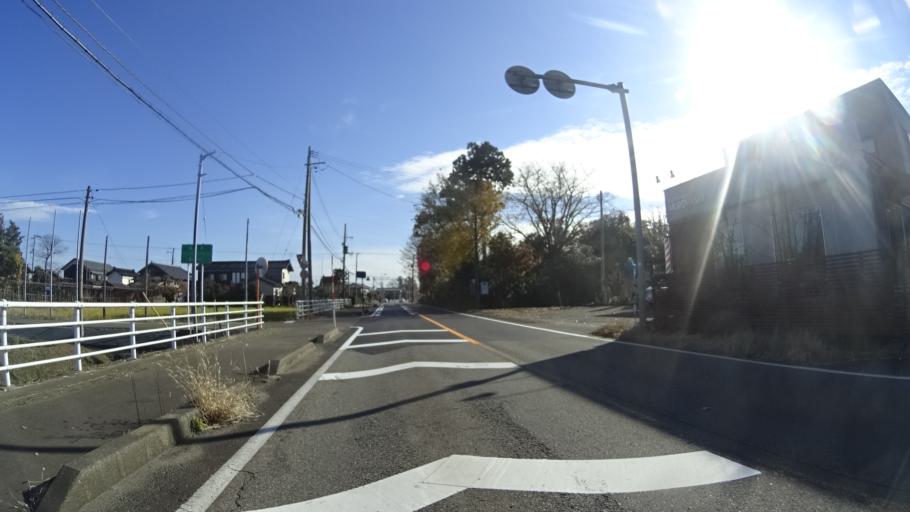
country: JP
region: Niigata
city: Mitsuke
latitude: 37.5547
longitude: 138.8540
